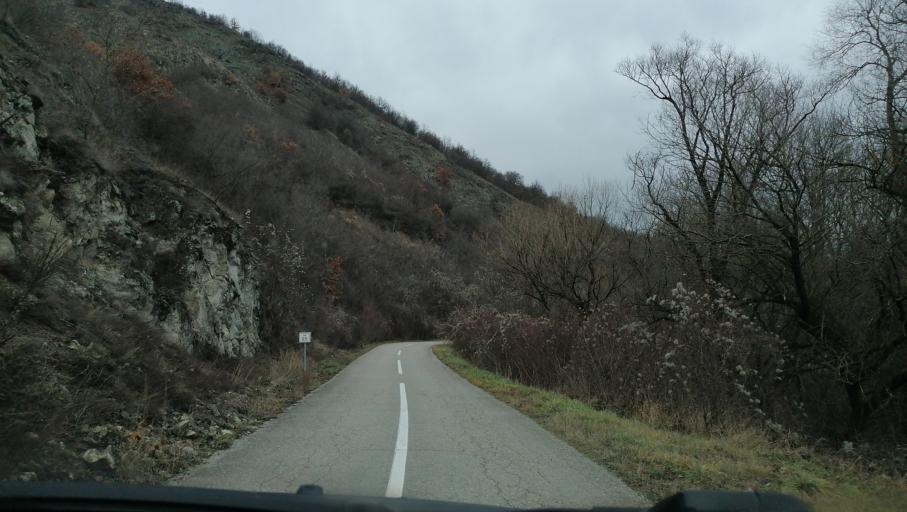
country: RS
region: Central Serbia
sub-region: Pirotski Okrug
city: Dimitrovgrad
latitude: 42.9488
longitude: 22.7685
